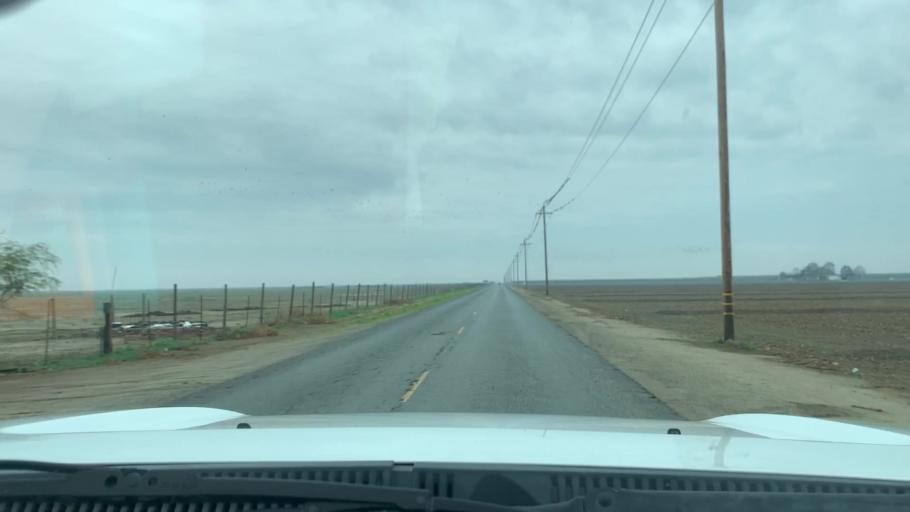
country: US
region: California
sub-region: Tulare County
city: Alpaugh
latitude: 35.7611
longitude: -119.4179
